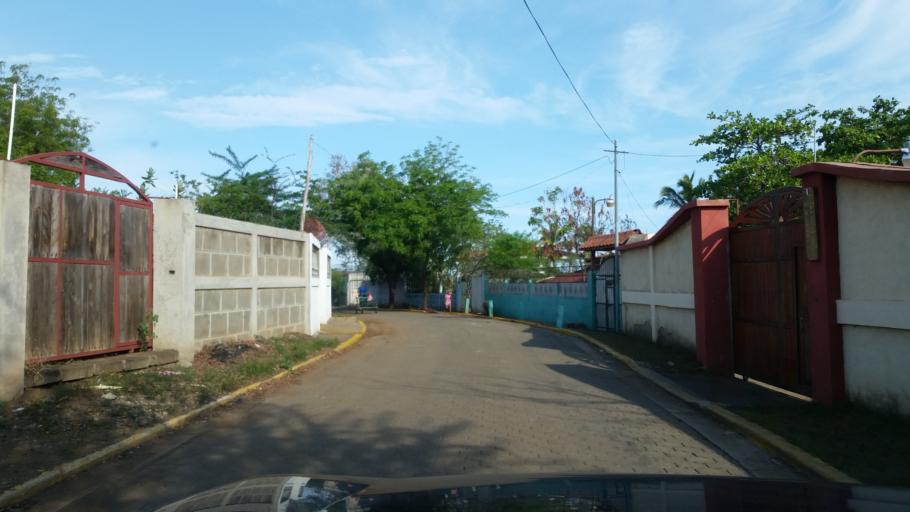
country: NI
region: Managua
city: Masachapa
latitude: 11.7771
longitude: -86.5158
